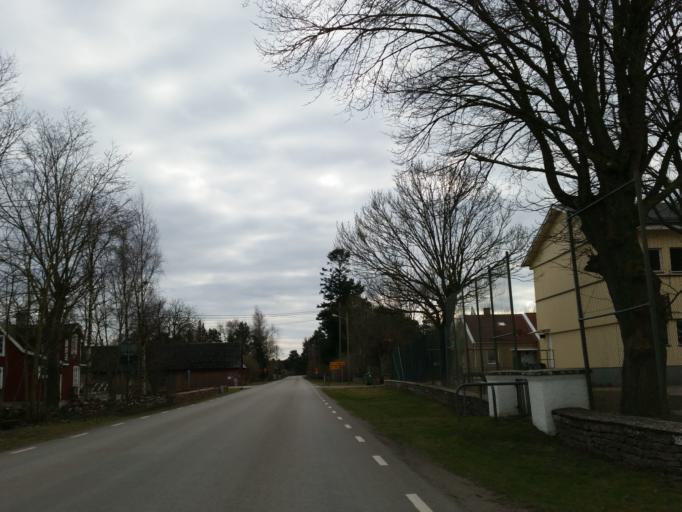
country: SE
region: Kalmar
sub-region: Morbylanga Kommun
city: Sodra Sandby
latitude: 56.5944
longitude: 16.6348
